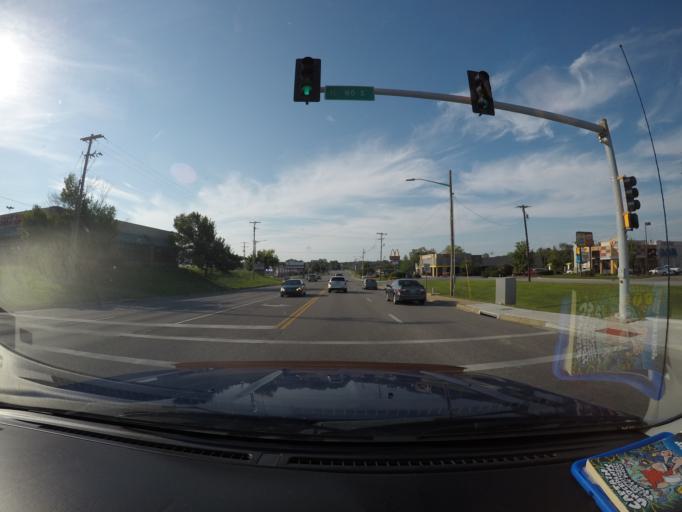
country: US
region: Kansas
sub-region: Leavenworth County
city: Leavenworth
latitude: 39.2850
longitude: -94.9043
